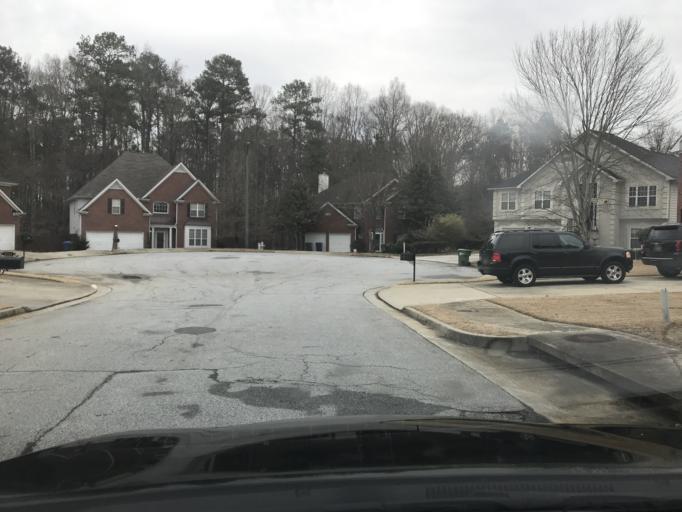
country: US
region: Georgia
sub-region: Fulton County
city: East Point
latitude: 33.7144
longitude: -84.5045
